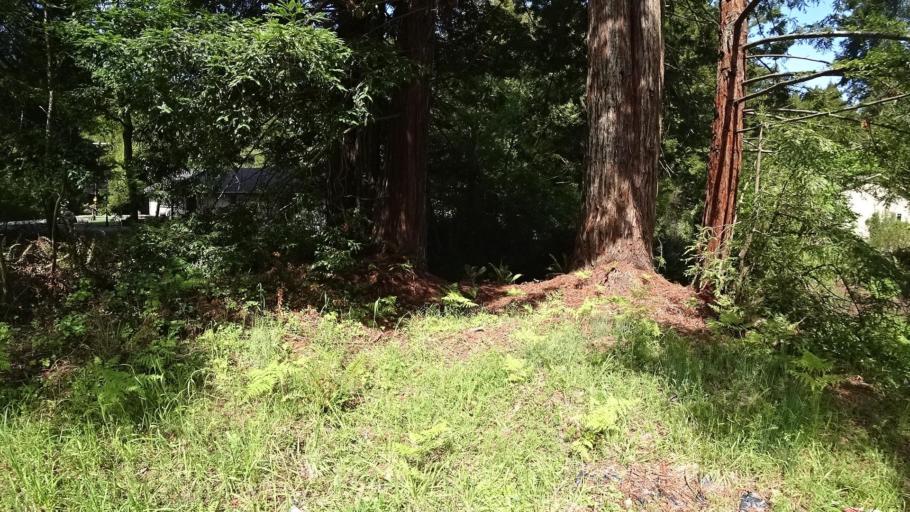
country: US
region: California
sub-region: Humboldt County
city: Fortuna
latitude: 40.6074
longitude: -124.1486
